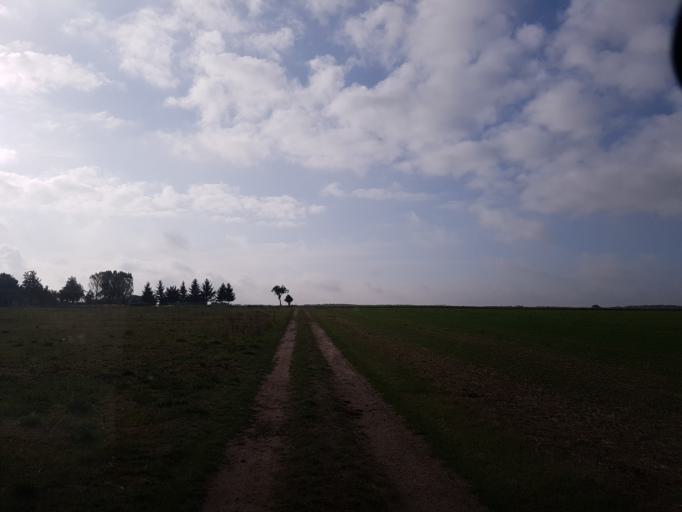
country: DE
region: Brandenburg
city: Finsterwalde
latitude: 51.6290
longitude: 13.7636
